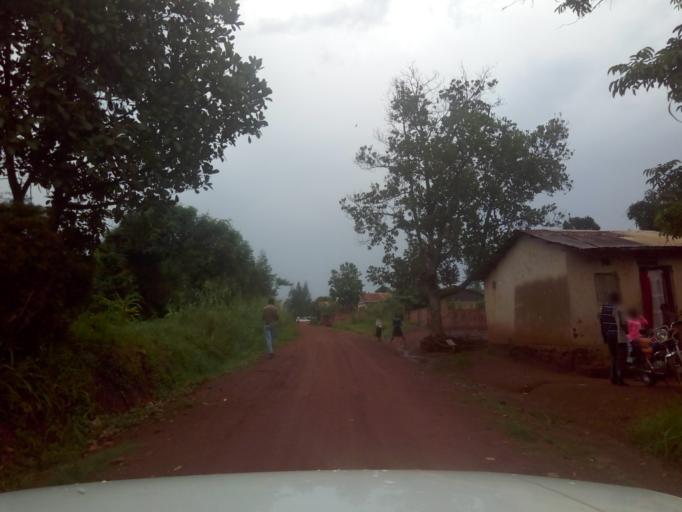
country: UG
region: Western Region
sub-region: Masindi District
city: Masindi
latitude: 1.6894
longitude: 31.7084
